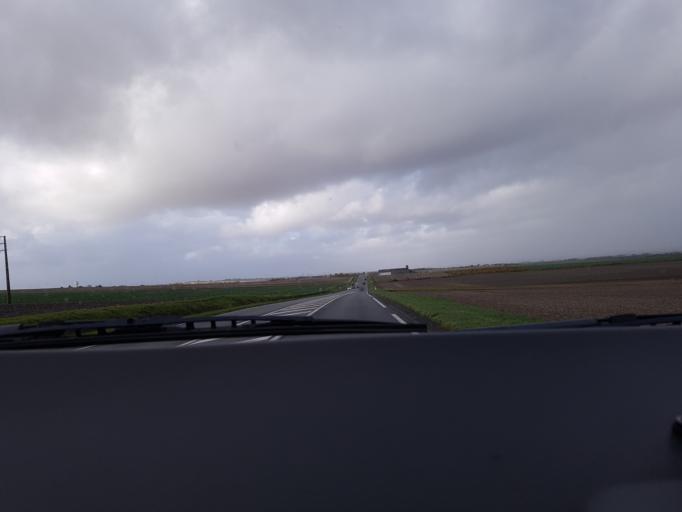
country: FR
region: Poitou-Charentes
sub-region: Departement de la Charente-Maritime
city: Pons
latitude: 45.6305
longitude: -0.5735
